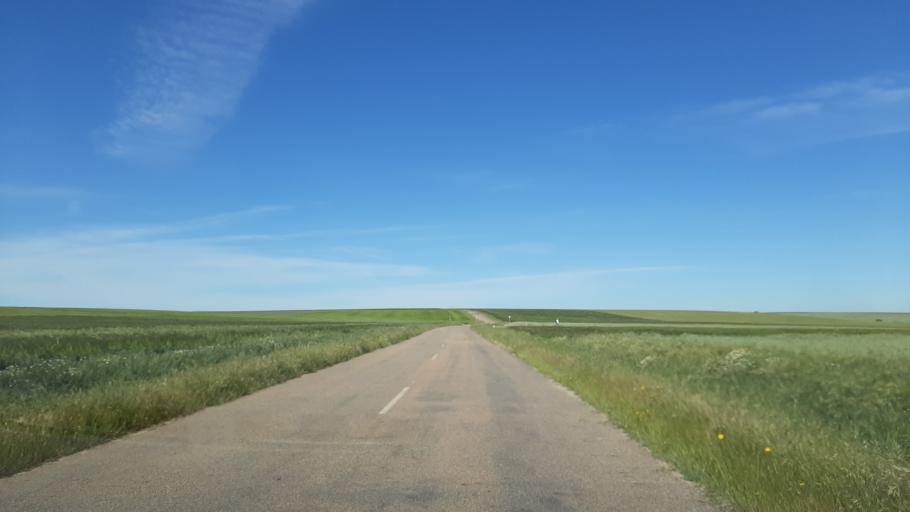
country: ES
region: Castille and Leon
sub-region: Provincia de Salamanca
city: Pedrosillo de Alba
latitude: 40.8230
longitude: -5.4051
